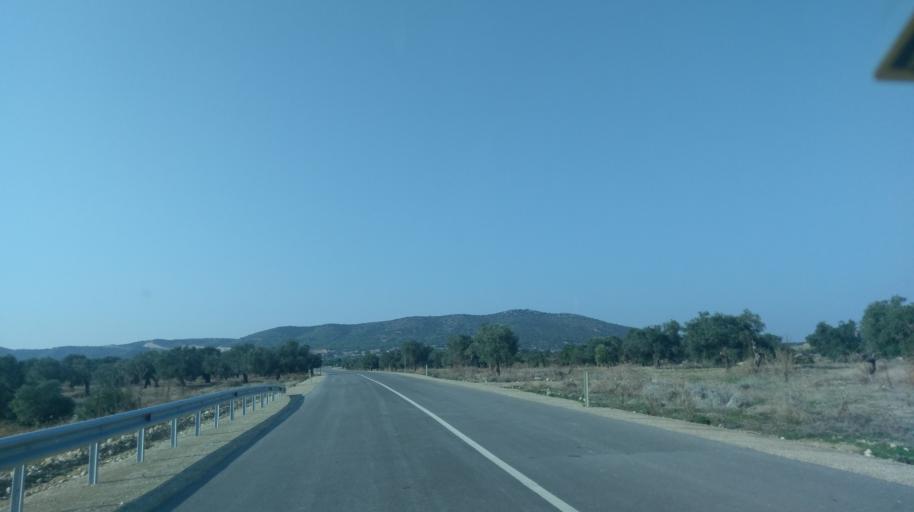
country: CY
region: Ammochostos
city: Rizokarpaso
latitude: 35.5253
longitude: 34.2868
